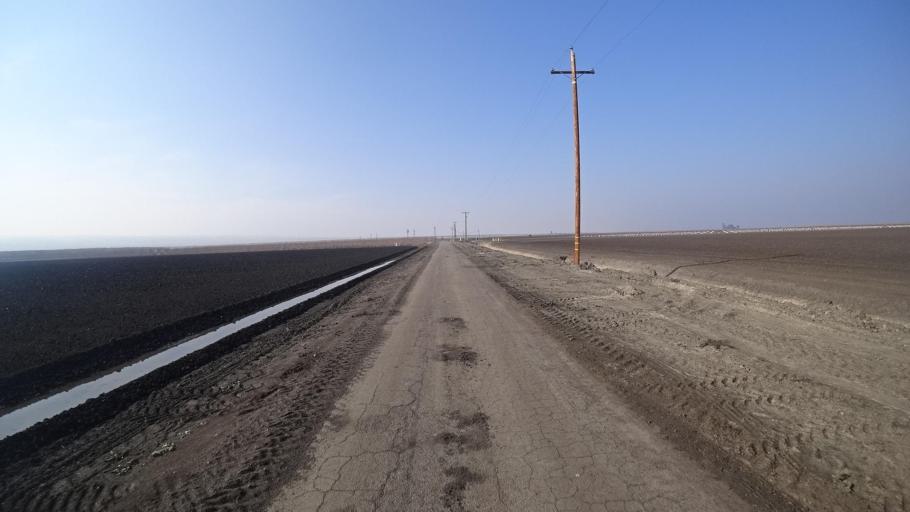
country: US
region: California
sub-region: Kern County
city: Buttonwillow
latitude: 35.3545
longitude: -119.4550
